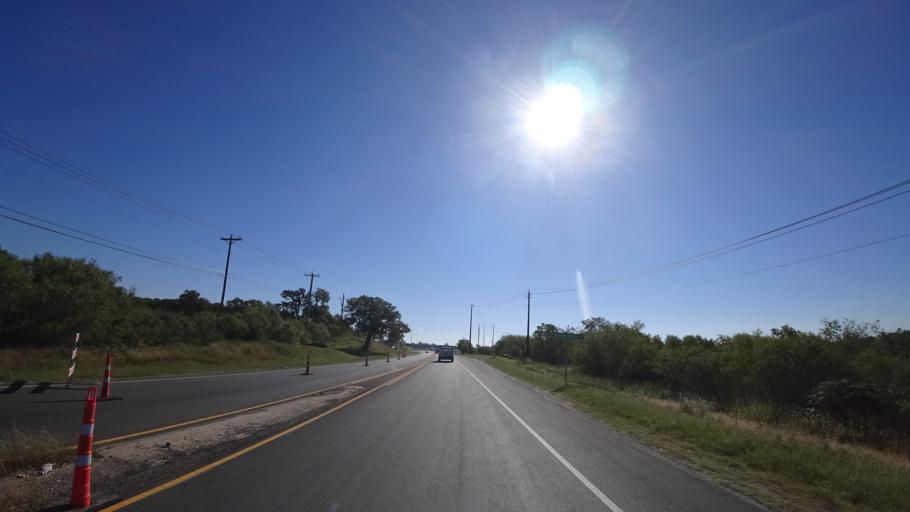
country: US
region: Texas
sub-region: Travis County
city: Hornsby Bend
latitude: 30.2554
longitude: -97.6092
